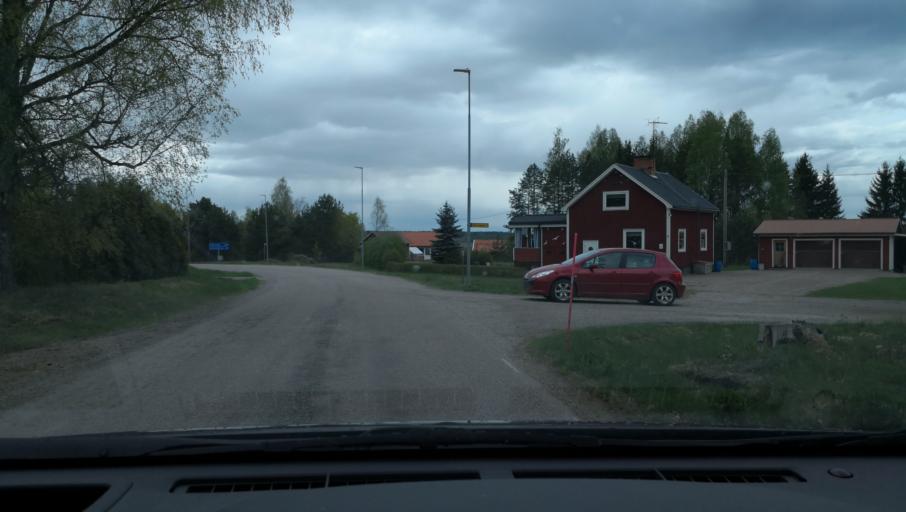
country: SE
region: Dalarna
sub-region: Avesta Kommun
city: Avesta
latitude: 60.0244
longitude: 16.3283
